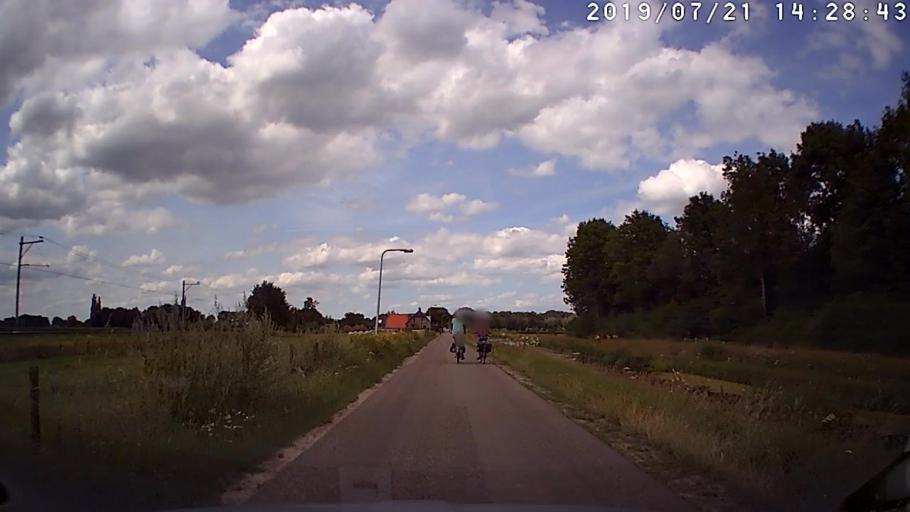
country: NL
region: Overijssel
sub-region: Gemeente Raalte
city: Heino
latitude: 52.4402
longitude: 6.2016
